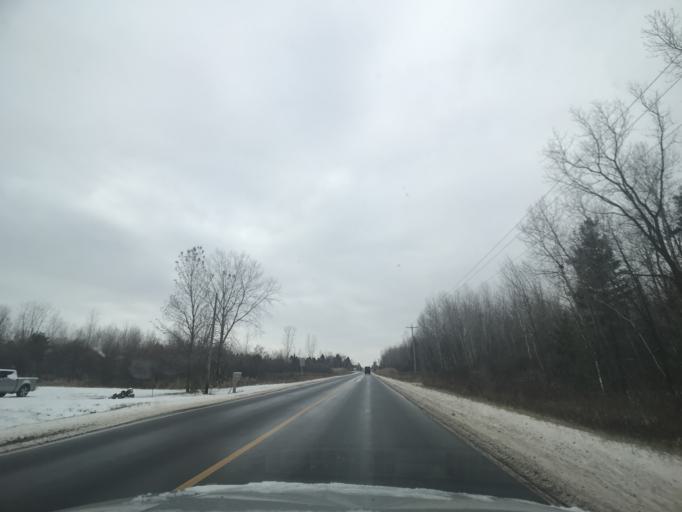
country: US
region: Wisconsin
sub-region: Brown County
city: Suamico
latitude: 44.7210
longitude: -88.0577
